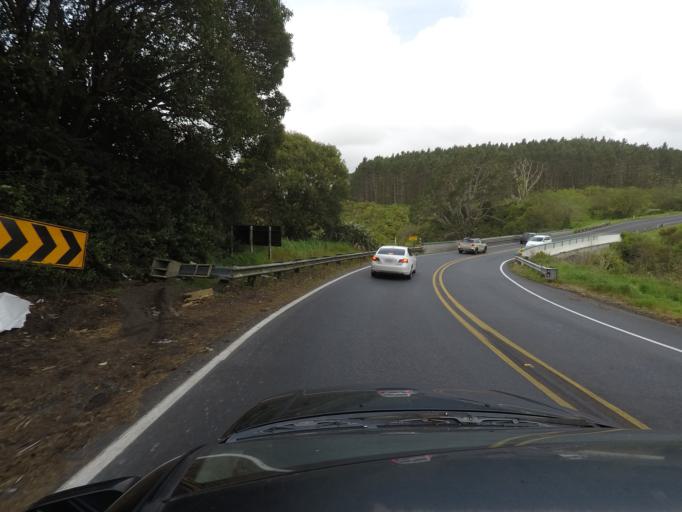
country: NZ
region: Auckland
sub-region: Auckland
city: Pakuranga
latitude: -36.9244
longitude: 174.9346
